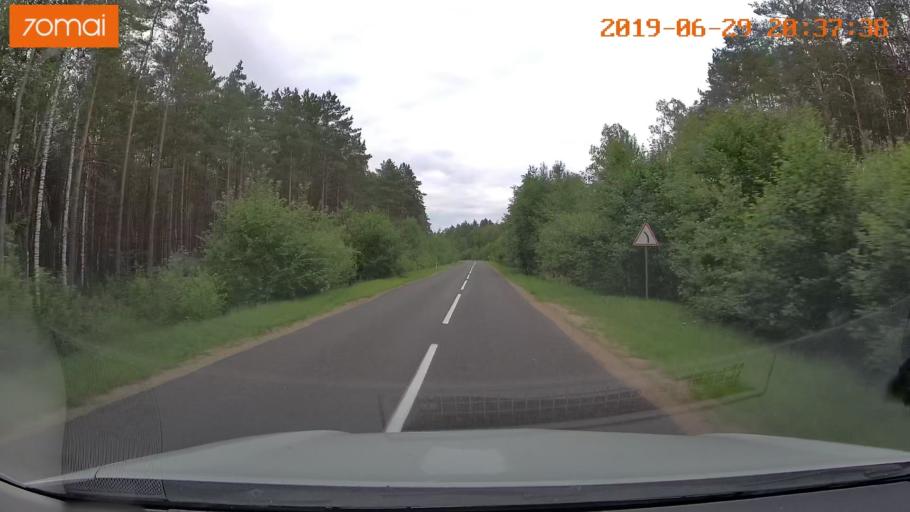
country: BY
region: Brest
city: Hantsavichy
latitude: 52.5405
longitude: 26.3652
